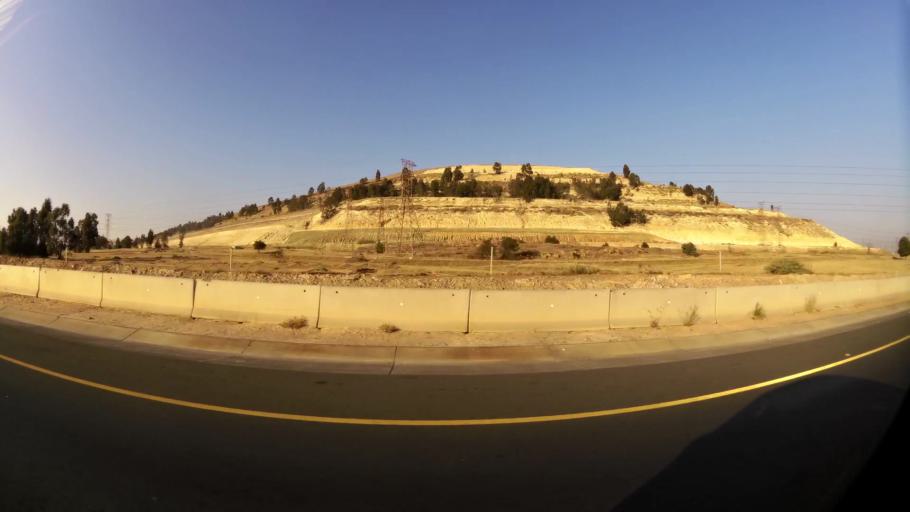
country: ZA
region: Gauteng
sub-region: City of Johannesburg Metropolitan Municipality
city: Johannesburg
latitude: -26.2170
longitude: 27.9530
